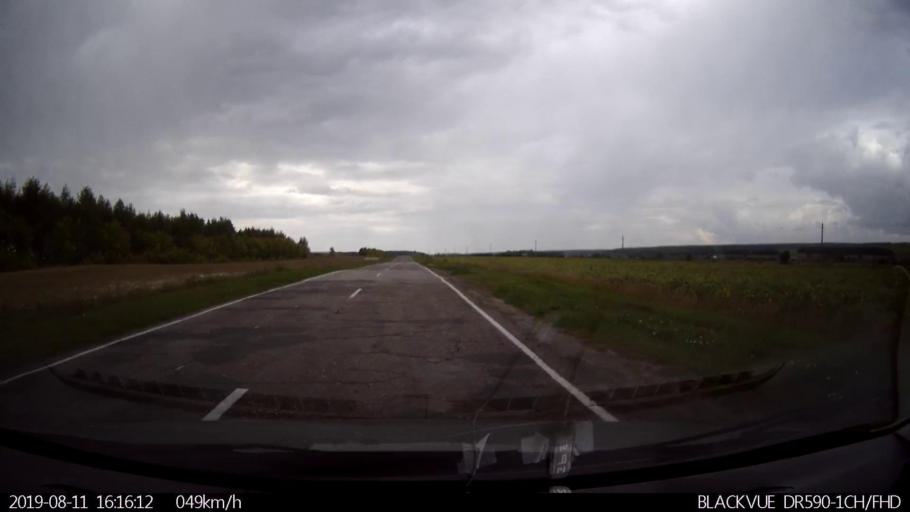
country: RU
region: Ulyanovsk
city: Mayna
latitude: 54.0394
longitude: 47.6225
